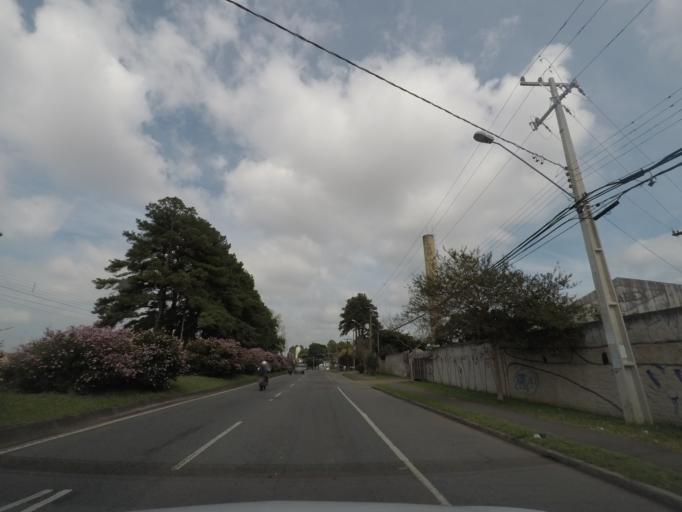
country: BR
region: Parana
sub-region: Curitiba
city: Curitiba
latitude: -25.4936
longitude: -49.3241
